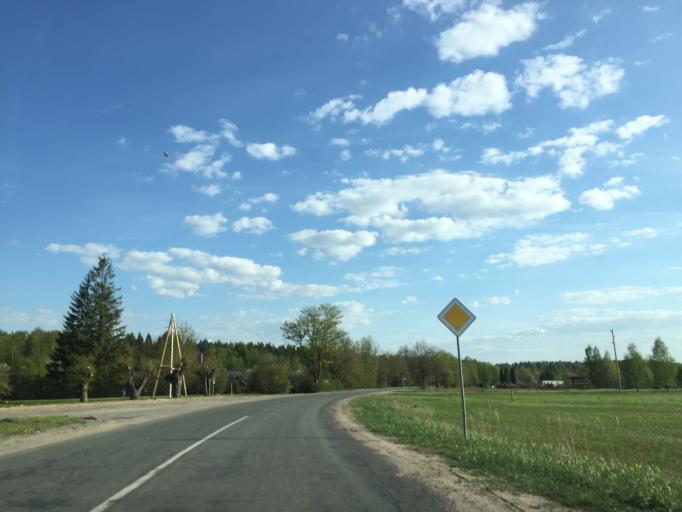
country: LV
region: Sigulda
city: Sigulda
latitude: 57.2551
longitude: 24.8742
